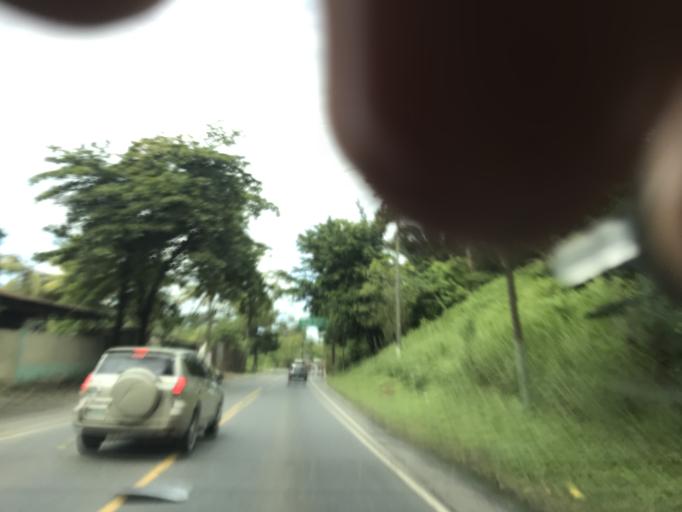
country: GT
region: Izabal
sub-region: Municipio de Puerto Barrios
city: Puerto Barrios
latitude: 15.6682
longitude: -88.5615
